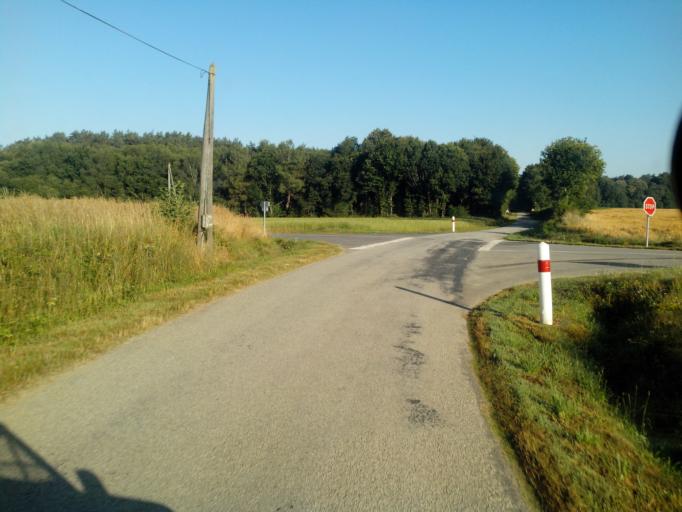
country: FR
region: Brittany
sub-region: Departement du Morbihan
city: Meneac
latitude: 48.1213
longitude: -2.4255
